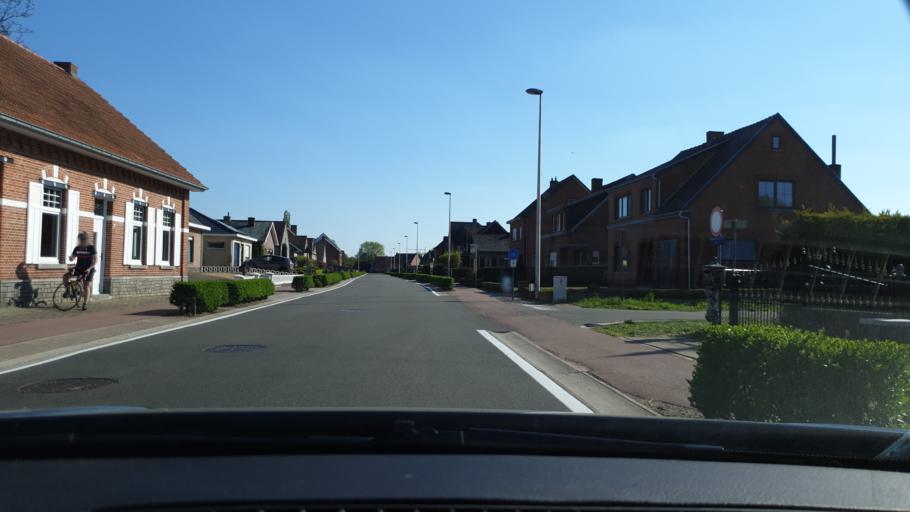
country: BE
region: Flanders
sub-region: Provincie Antwerpen
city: Laakdal
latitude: 51.0841
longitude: 5.0185
